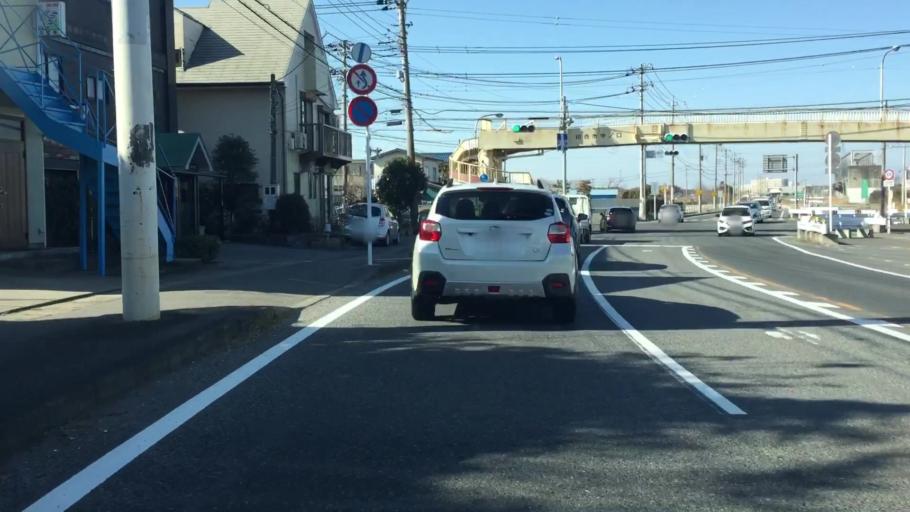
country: JP
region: Ibaraki
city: Ryugasaki
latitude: 35.8353
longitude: 140.1384
